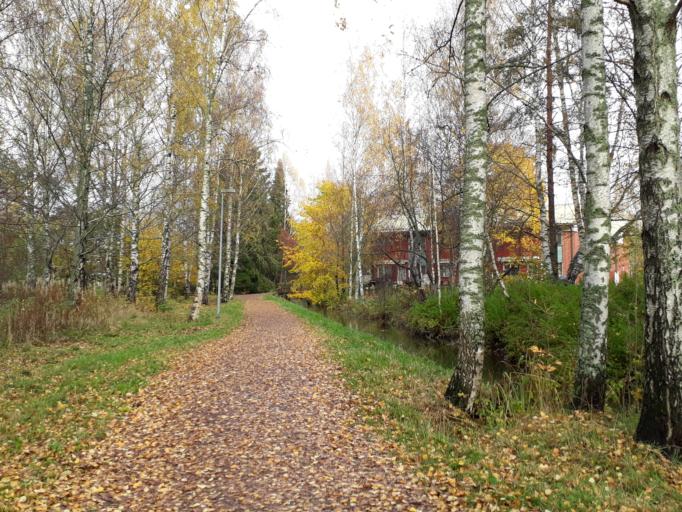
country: FI
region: Uusimaa
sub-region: Helsinki
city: Espoo
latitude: 60.1967
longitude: 24.6831
